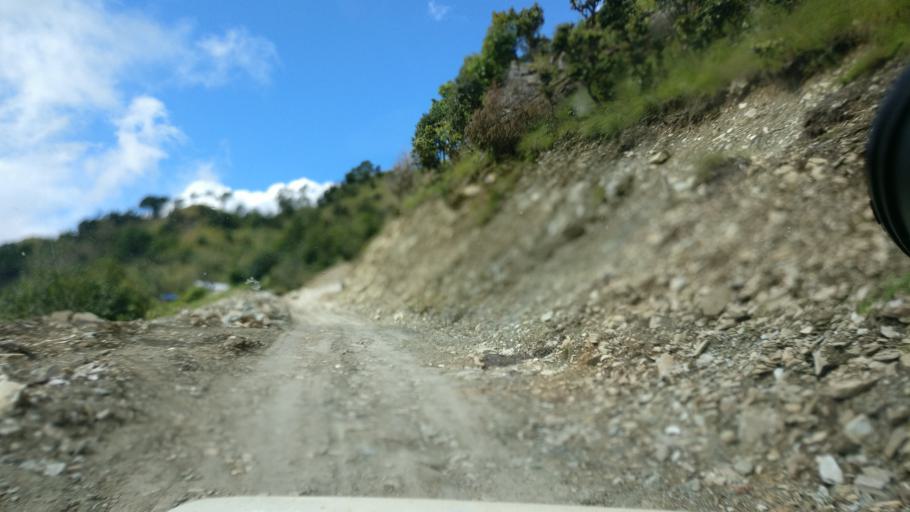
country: NP
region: Western Region
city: Baglung
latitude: 28.2829
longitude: 83.6391
